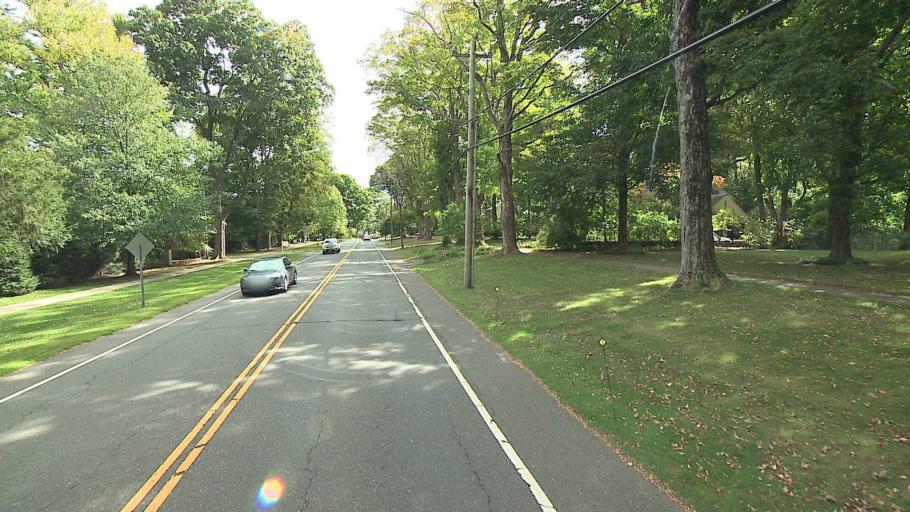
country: US
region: Connecticut
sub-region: Fairfield County
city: Ridgefield
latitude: 41.2702
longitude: -73.4958
